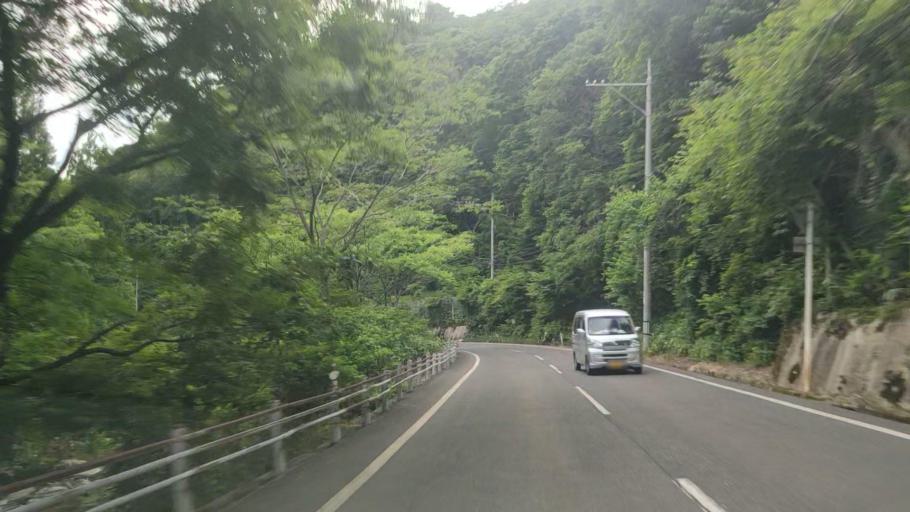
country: JP
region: Tottori
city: Kurayoshi
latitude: 35.2925
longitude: 133.9883
